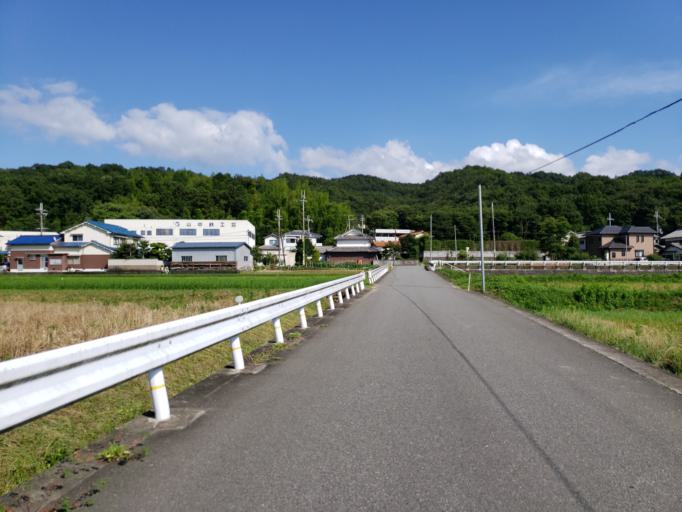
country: JP
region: Hyogo
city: Himeji
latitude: 34.9068
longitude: 134.7703
